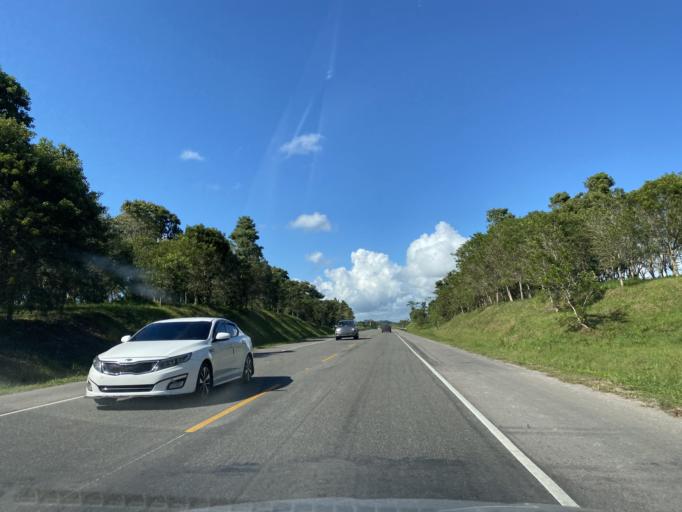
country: DO
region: Monte Plata
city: Majagual
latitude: 18.9933
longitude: -69.8146
